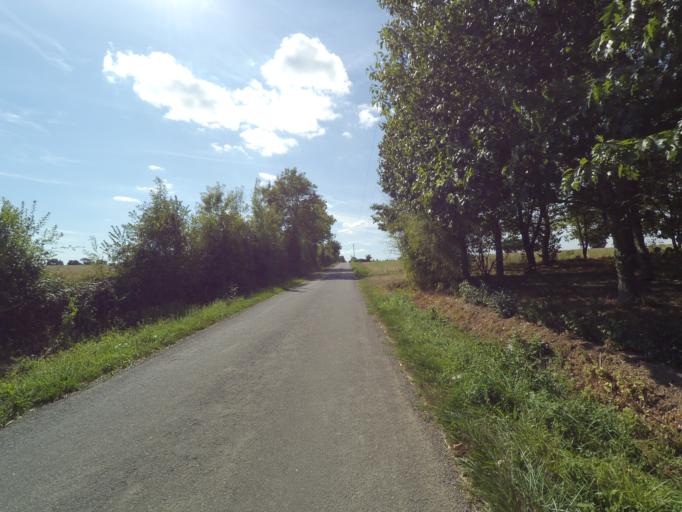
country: FR
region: Pays de la Loire
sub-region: Departement de la Loire-Atlantique
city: Vieillevigne
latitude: 46.9596
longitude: -1.4343
